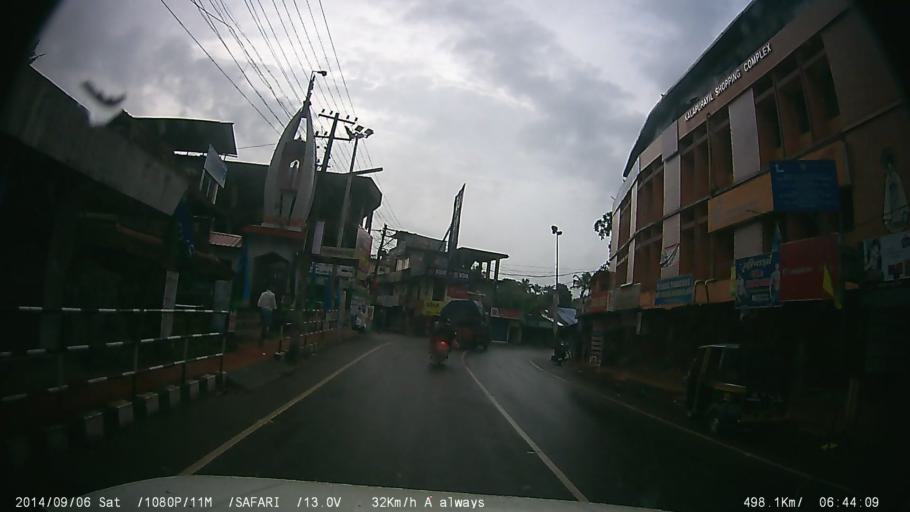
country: IN
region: Kerala
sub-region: Kottayam
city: Vaikam
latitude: 9.7682
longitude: 76.4901
